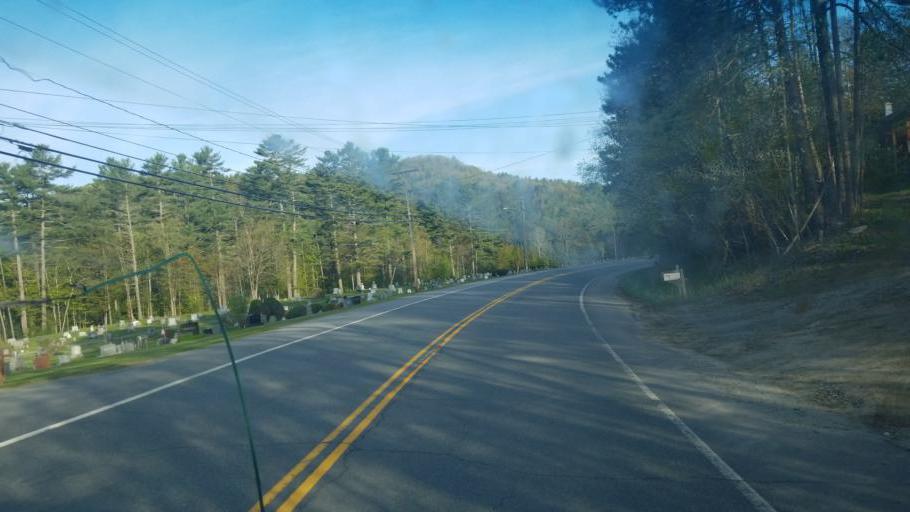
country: US
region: New Hampshire
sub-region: Grafton County
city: Littleton
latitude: 44.3122
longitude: -71.7920
